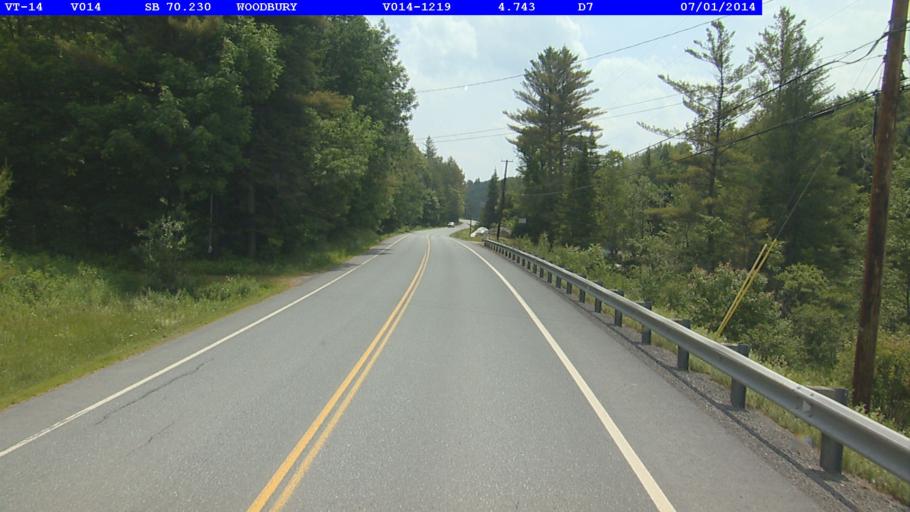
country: US
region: Vermont
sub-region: Caledonia County
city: Hardwick
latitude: 44.4557
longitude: -72.4201
